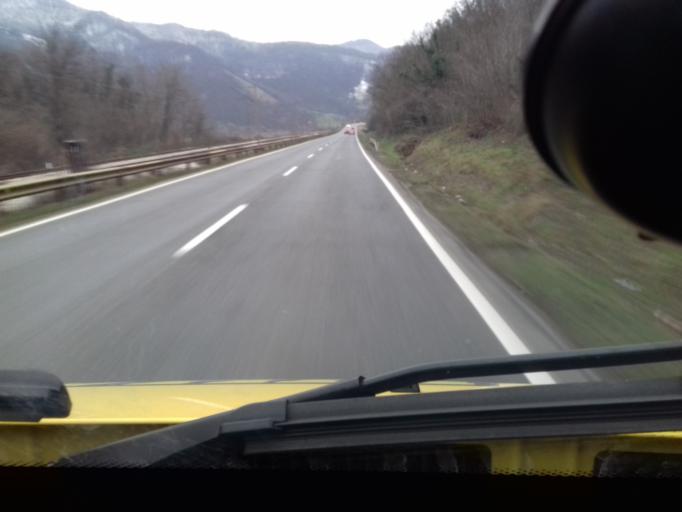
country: BA
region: Federation of Bosnia and Herzegovina
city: Zepce
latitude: 44.4092
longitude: 18.0003
